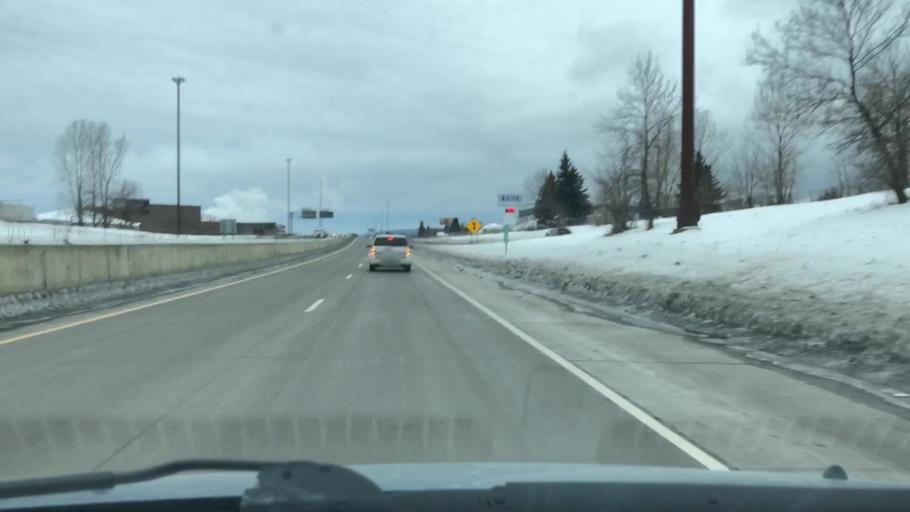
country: US
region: Wisconsin
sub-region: Douglas County
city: Superior
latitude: 46.7425
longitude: -92.1552
